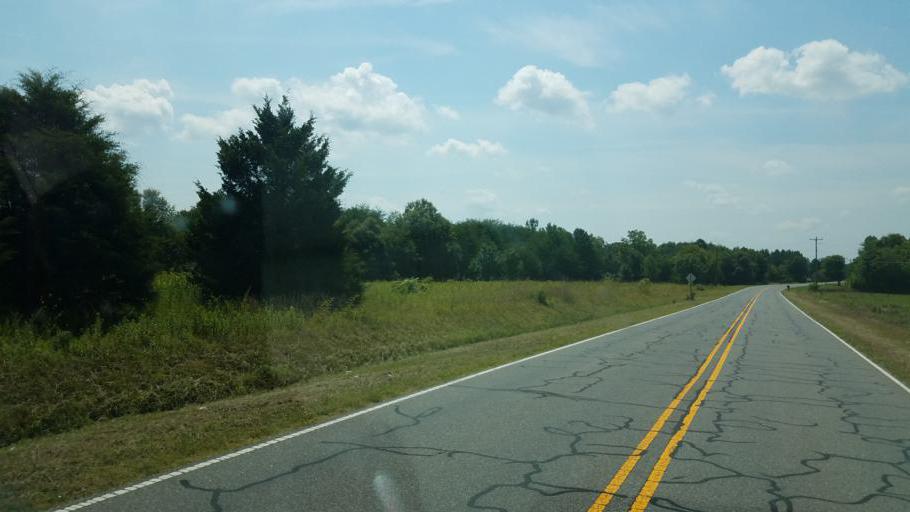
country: US
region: North Carolina
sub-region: Gaston County
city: Cherryville
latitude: 35.4540
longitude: -81.4309
